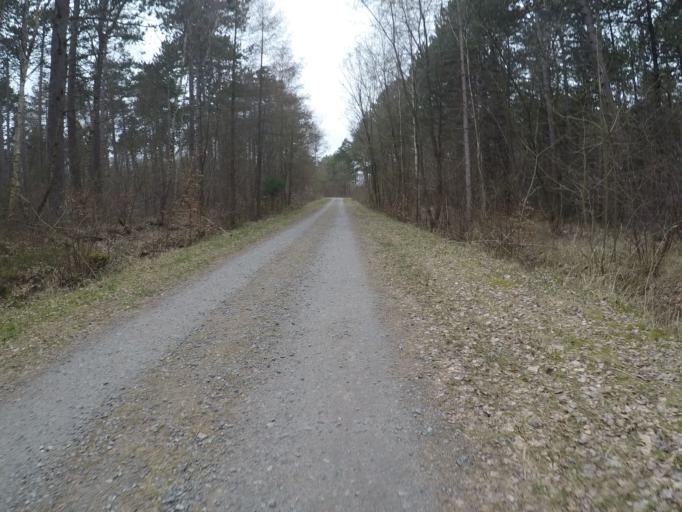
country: DE
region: Lower Saxony
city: Nordholz
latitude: 53.8191
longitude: 8.6400
